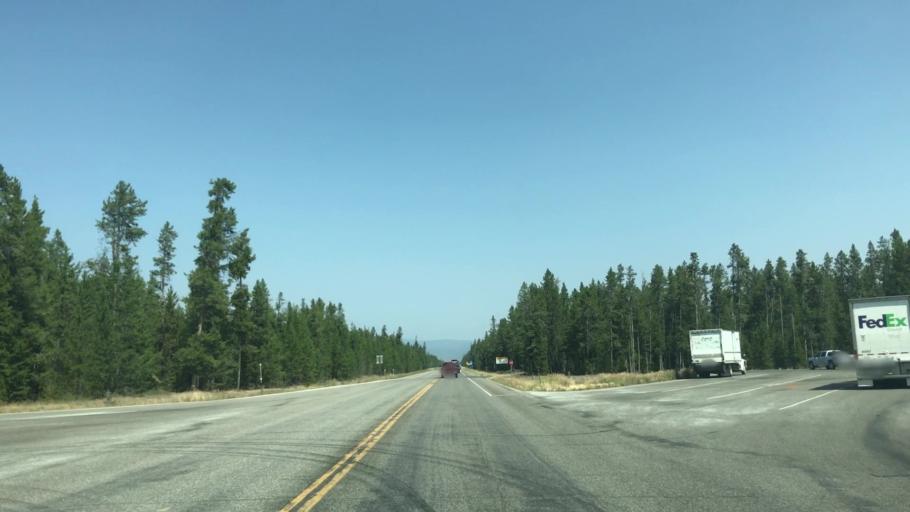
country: US
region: Montana
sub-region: Gallatin County
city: West Yellowstone
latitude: 44.6738
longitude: -111.1003
